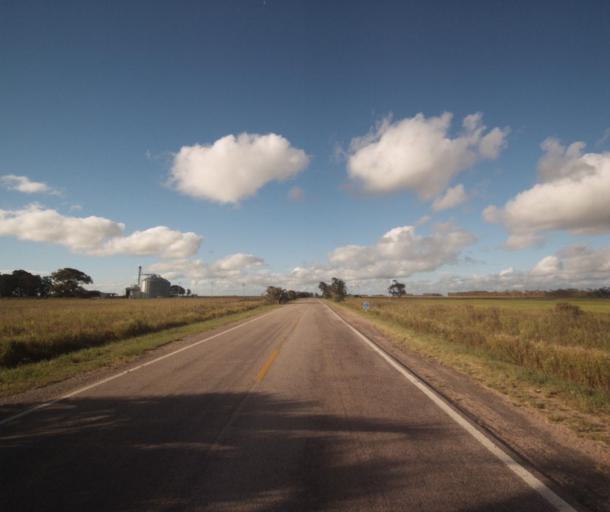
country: BR
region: Rio Grande do Sul
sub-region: Arroio Grande
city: Arroio Grande
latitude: -32.4467
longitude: -52.5695
